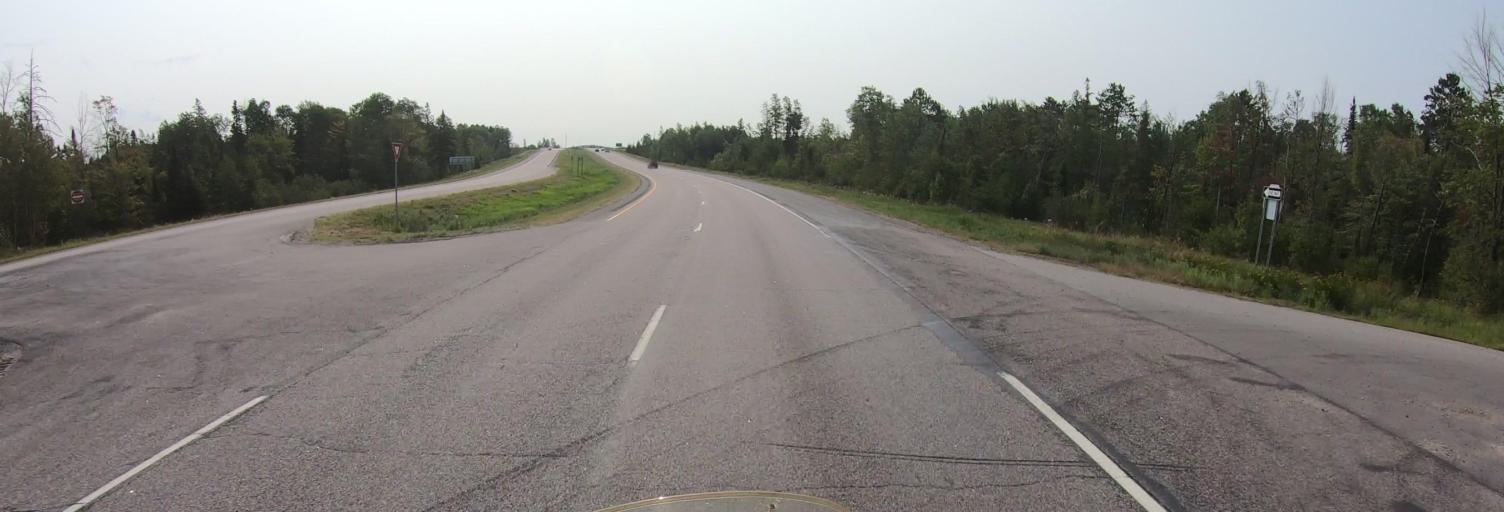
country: US
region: Minnesota
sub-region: Saint Louis County
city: Parkville
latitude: 47.5935
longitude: -92.5528
